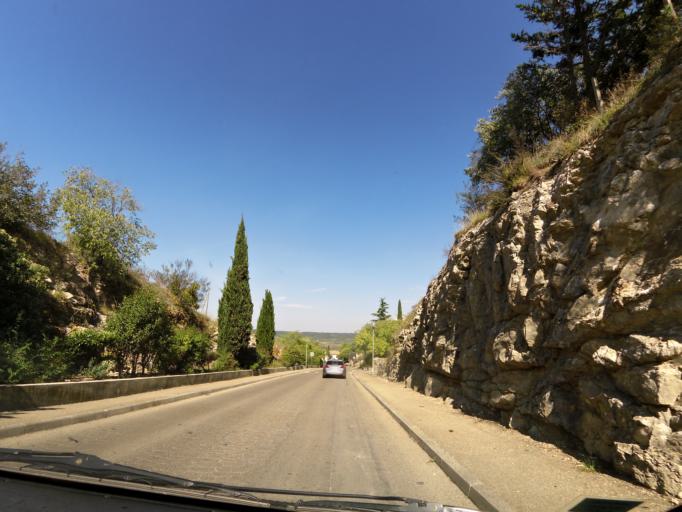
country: FR
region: Languedoc-Roussillon
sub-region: Departement du Gard
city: Langlade
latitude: 43.8032
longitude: 4.2522
